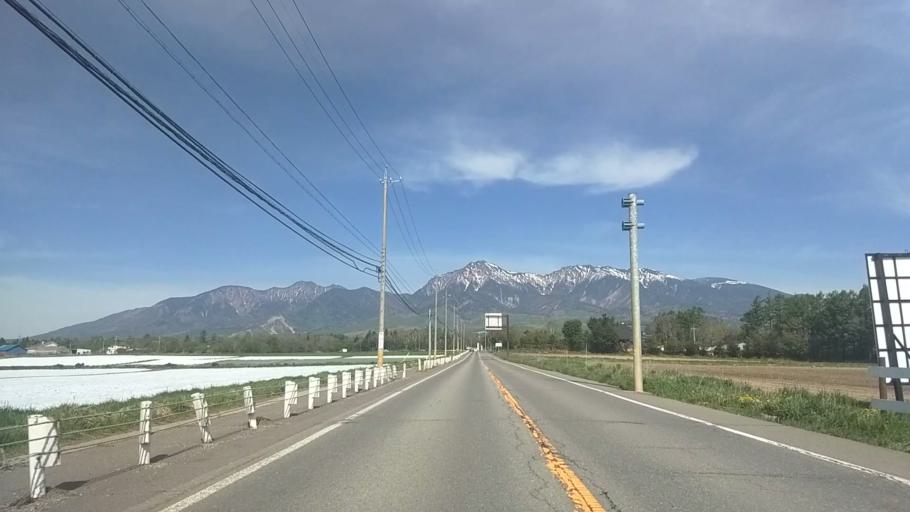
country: JP
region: Yamanashi
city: Nirasaki
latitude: 35.9561
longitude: 138.4695
